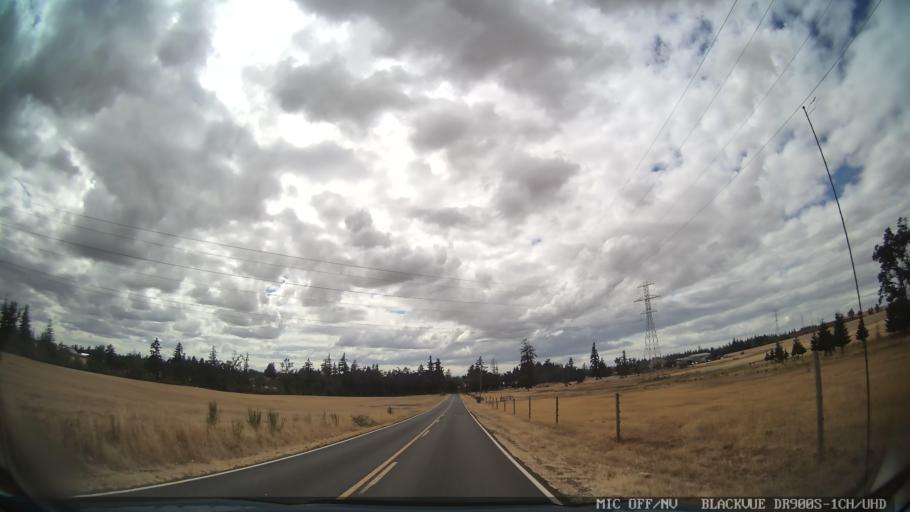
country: US
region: Oregon
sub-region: Marion County
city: Sublimity
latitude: 44.8443
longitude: -122.7682
